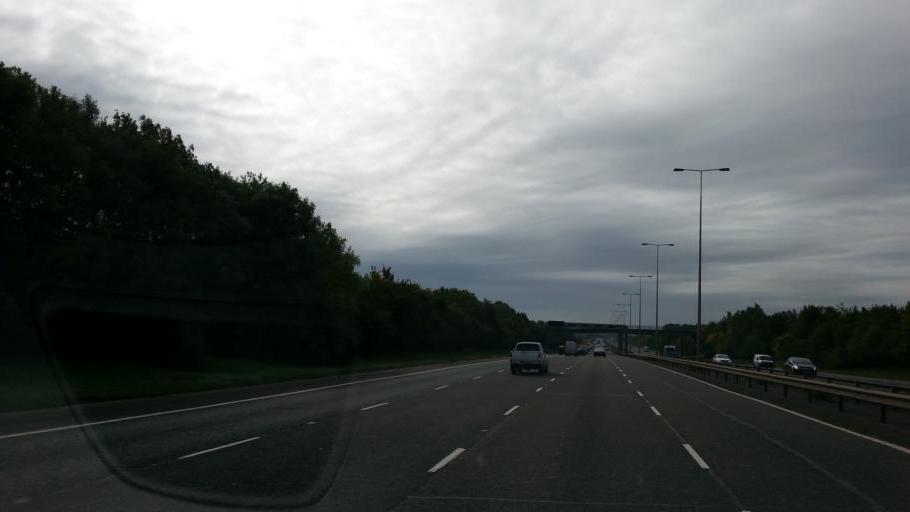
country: GB
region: England
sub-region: Cambridgeshire
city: Sawtry
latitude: 52.4413
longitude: -0.2743
